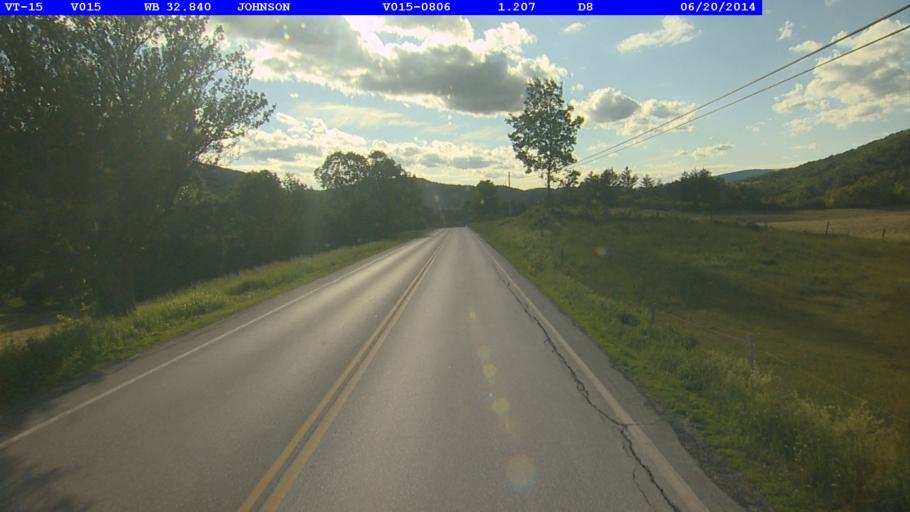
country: US
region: Vermont
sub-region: Lamoille County
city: Johnson
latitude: 44.6458
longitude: -72.7312
